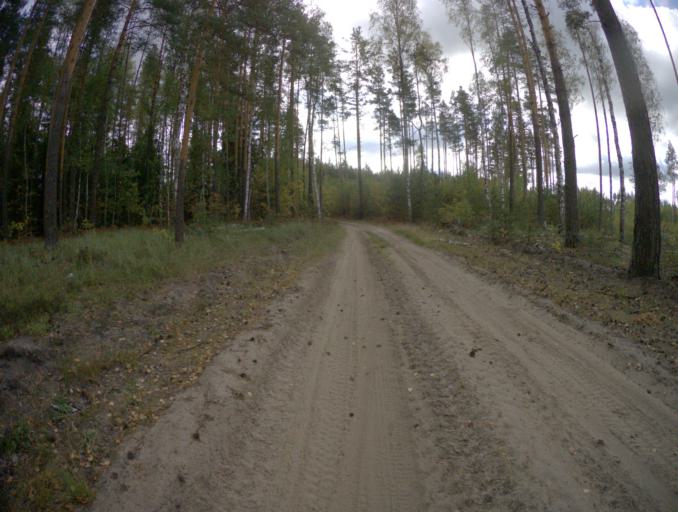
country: RU
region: Moskovskaya
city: Baksheyevo
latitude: 55.7146
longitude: 39.8507
